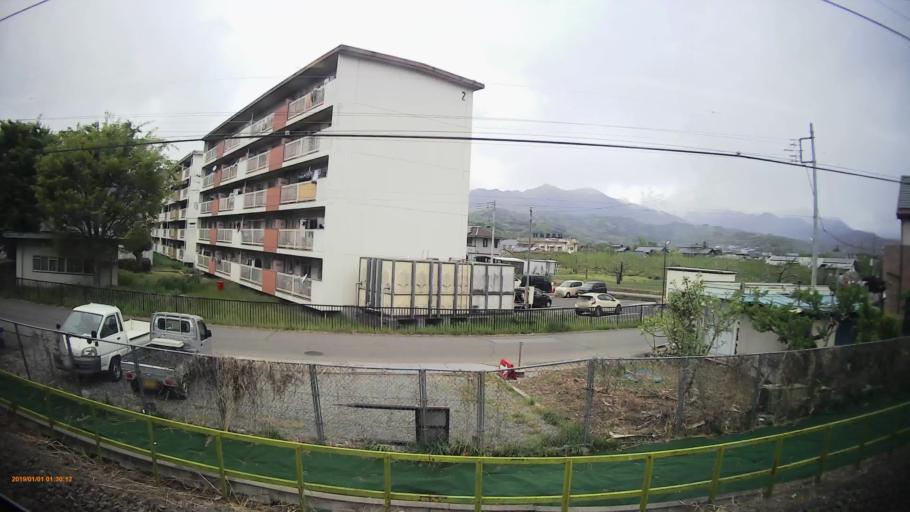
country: JP
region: Yamanashi
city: Enzan
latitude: 35.6950
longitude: 138.7042
